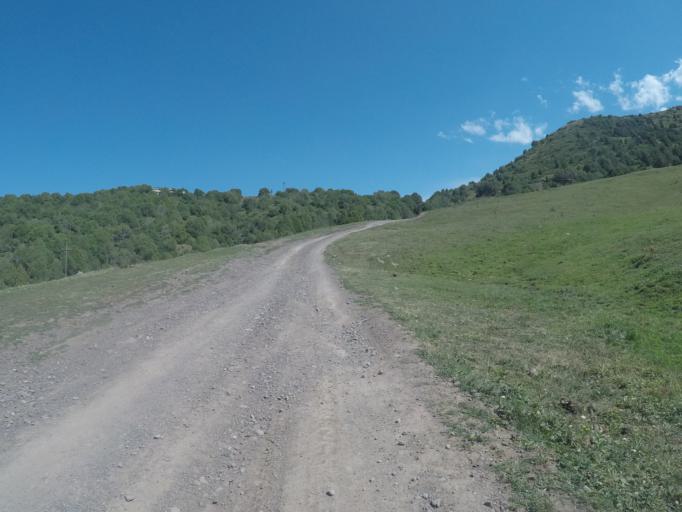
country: KG
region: Chuy
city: Bishkek
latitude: 42.6478
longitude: 74.5577
